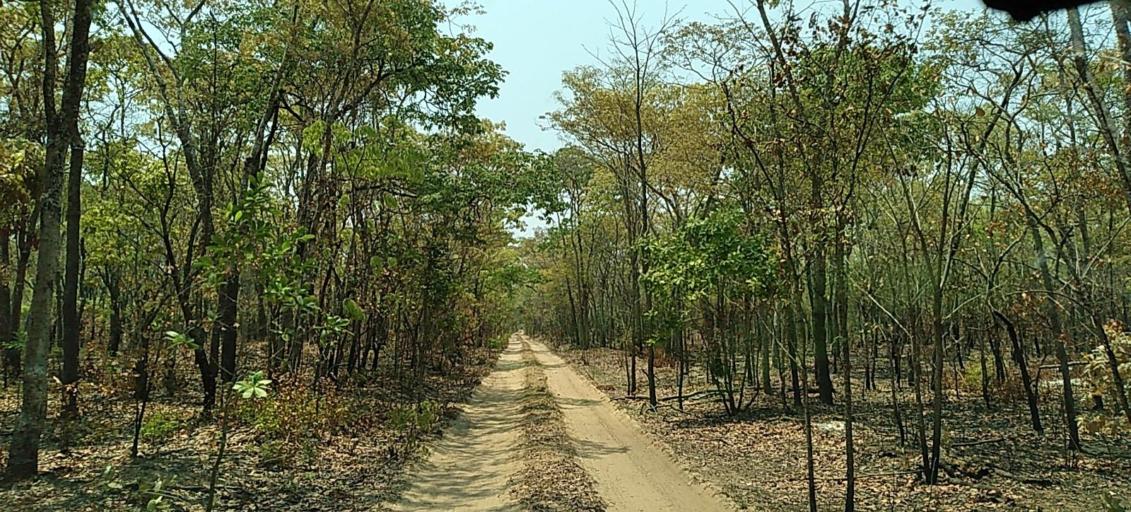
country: ZM
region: North-Western
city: Kabompo
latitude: -13.6473
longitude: 24.4794
